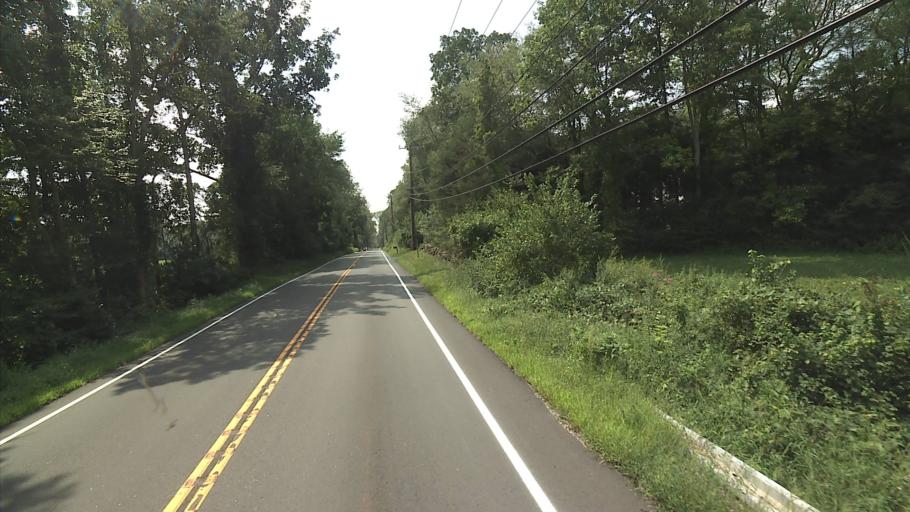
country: US
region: Connecticut
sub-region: New London County
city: Montville Center
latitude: 41.4827
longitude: -72.2569
